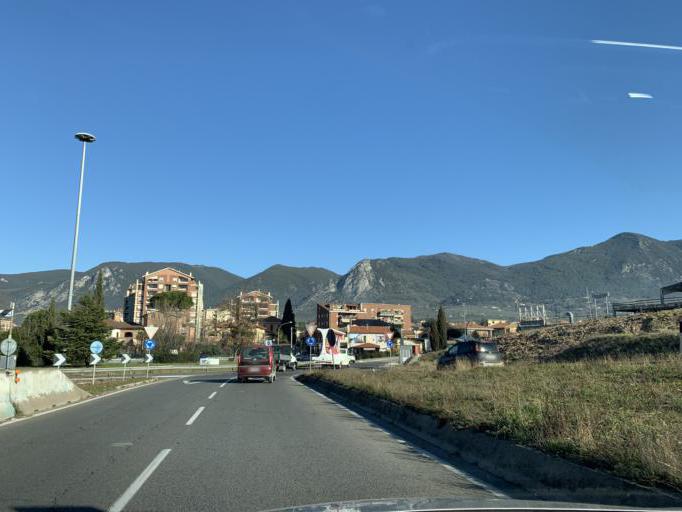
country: IT
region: Umbria
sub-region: Provincia di Terni
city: Terni
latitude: 42.5754
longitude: 12.6266
